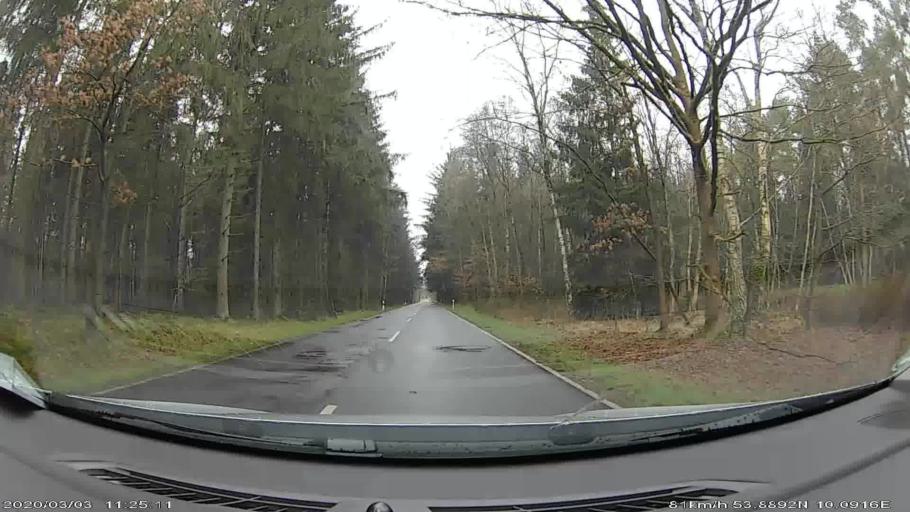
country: DE
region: Schleswig-Holstein
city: Hartenholm
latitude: 53.8913
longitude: 10.0871
